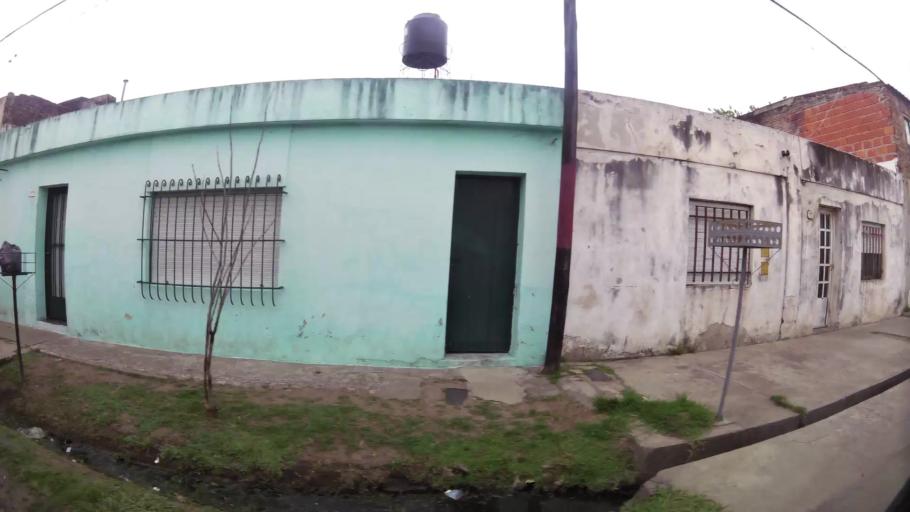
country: AR
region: Santa Fe
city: Gobernador Galvez
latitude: -32.9982
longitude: -60.6679
